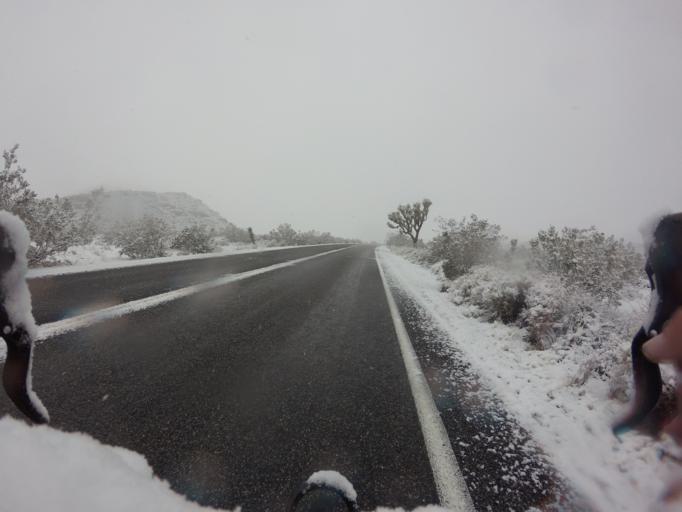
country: US
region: California
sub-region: San Bernardino County
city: Twentynine Palms
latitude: 34.0086
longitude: -116.0410
